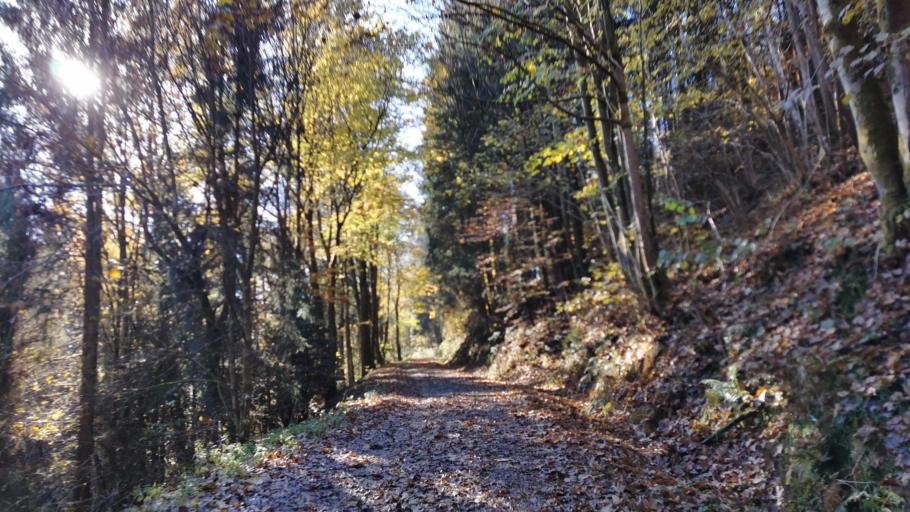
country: DE
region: Bavaria
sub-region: Upper Franconia
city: Nordhalben
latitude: 50.3888
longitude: 11.5287
